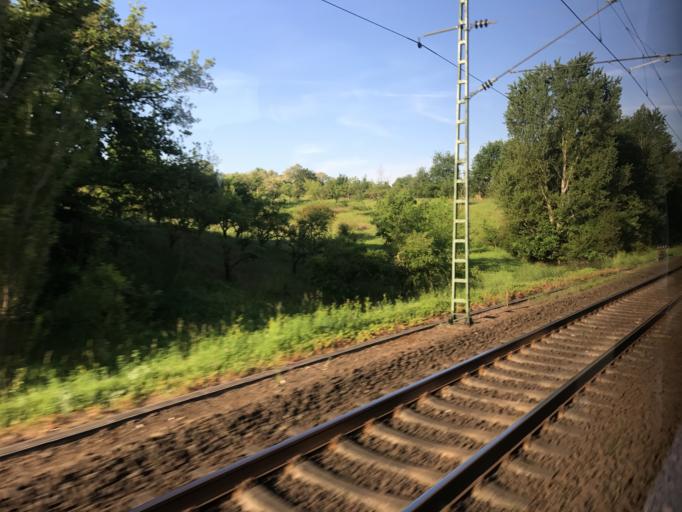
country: DE
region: Rheinland-Pfalz
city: Nieder-Ingelheim
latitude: 49.9941
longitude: 8.0929
